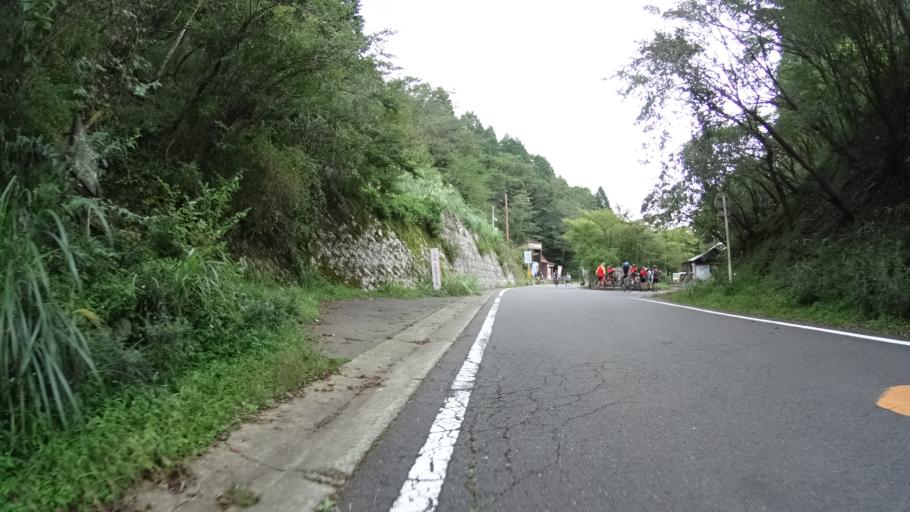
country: JP
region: Kanagawa
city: Hadano
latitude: 35.4276
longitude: 139.2197
